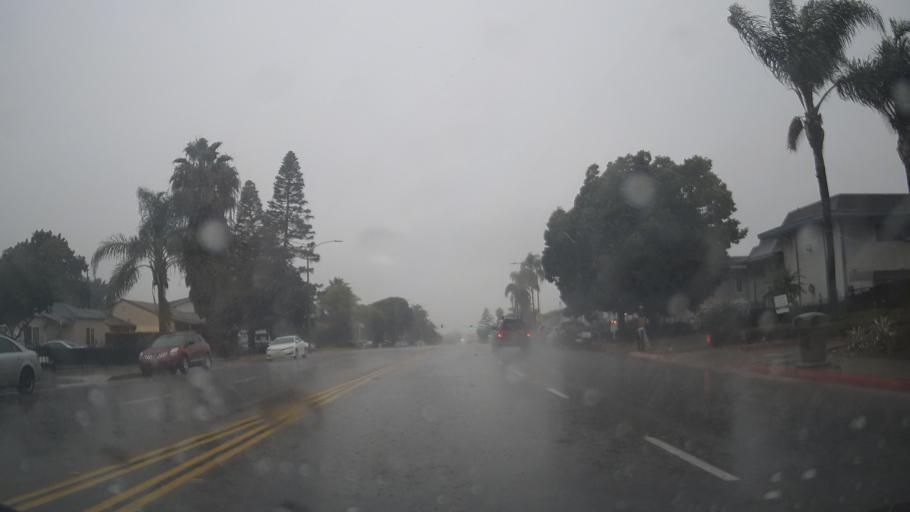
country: US
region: California
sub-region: San Diego County
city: Chula Vista
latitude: 32.6444
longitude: -117.0856
